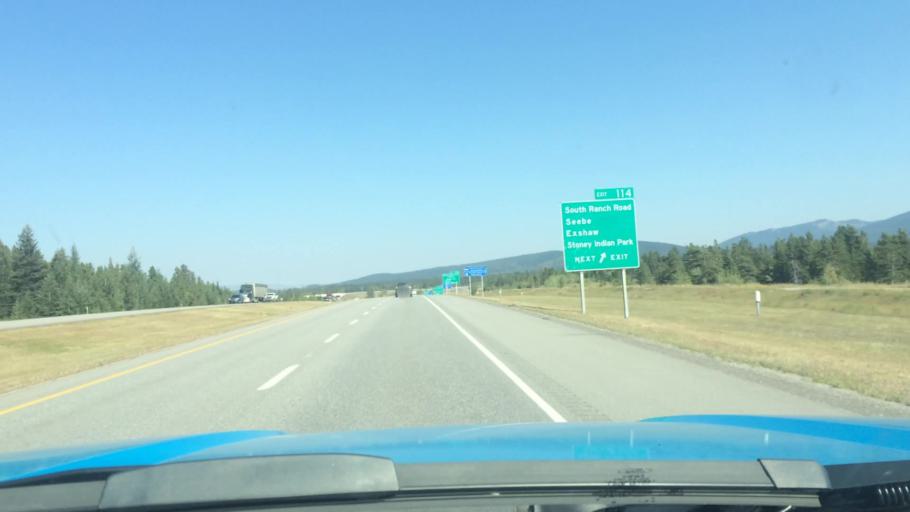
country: CA
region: Alberta
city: Canmore
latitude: 51.0724
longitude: -115.0699
